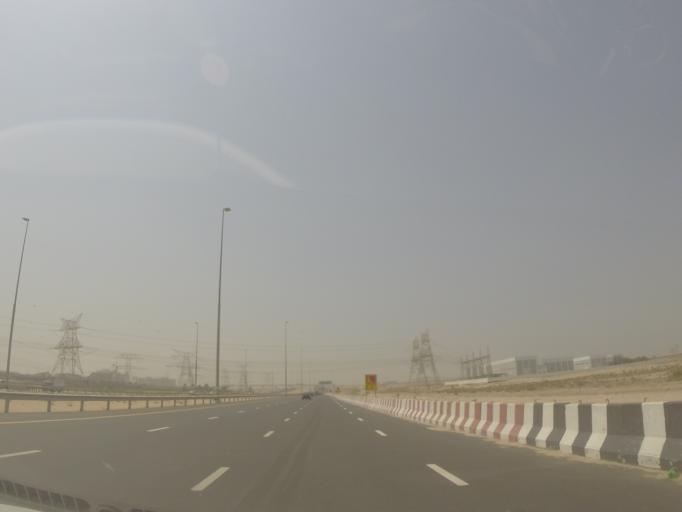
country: AE
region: Dubai
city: Dubai
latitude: 25.0071
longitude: 55.1709
